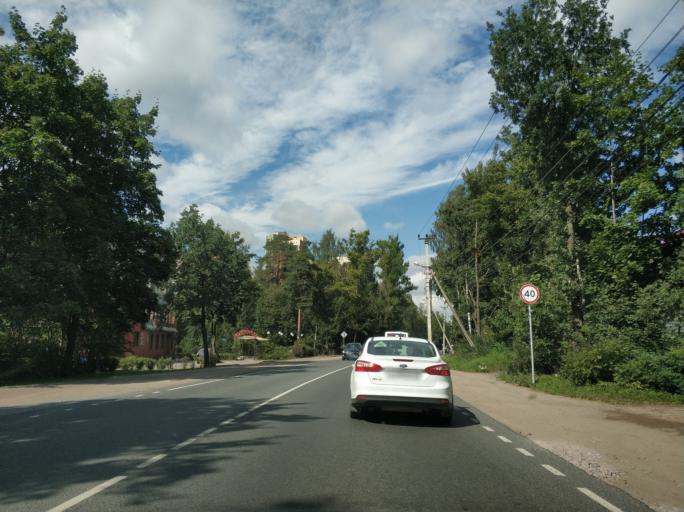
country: RU
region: Leningrad
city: Vsevolozhsk
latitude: 60.0301
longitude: 30.6390
